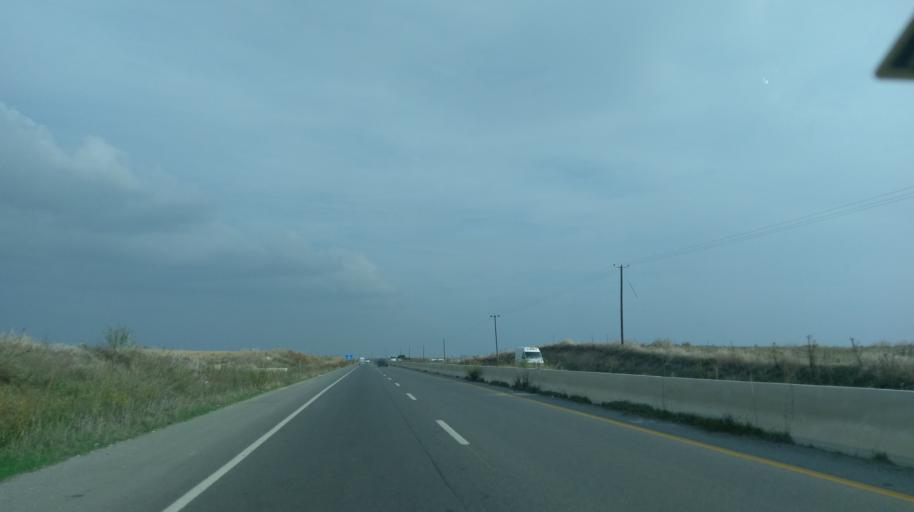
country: CY
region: Lefkosia
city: Mammari
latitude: 35.2116
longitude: 33.2117
